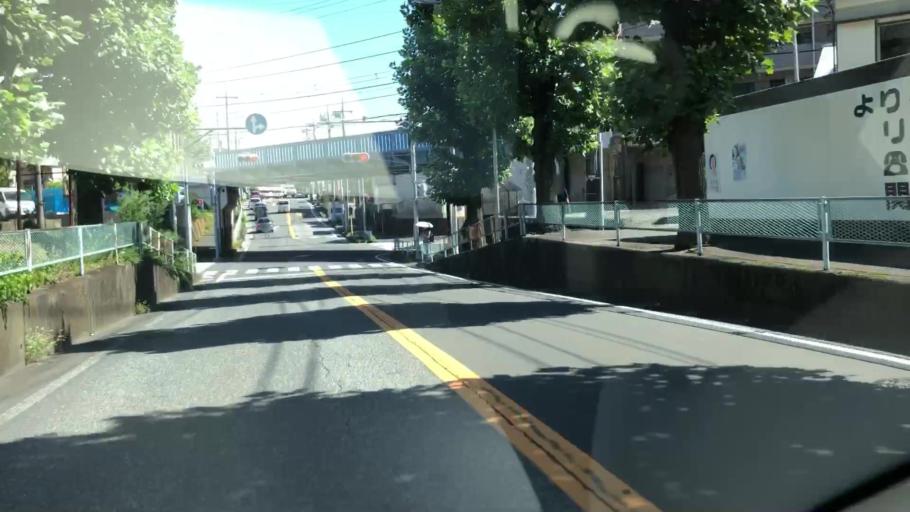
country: JP
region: Kanagawa
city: Yokohama
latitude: 35.3789
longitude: 139.6079
